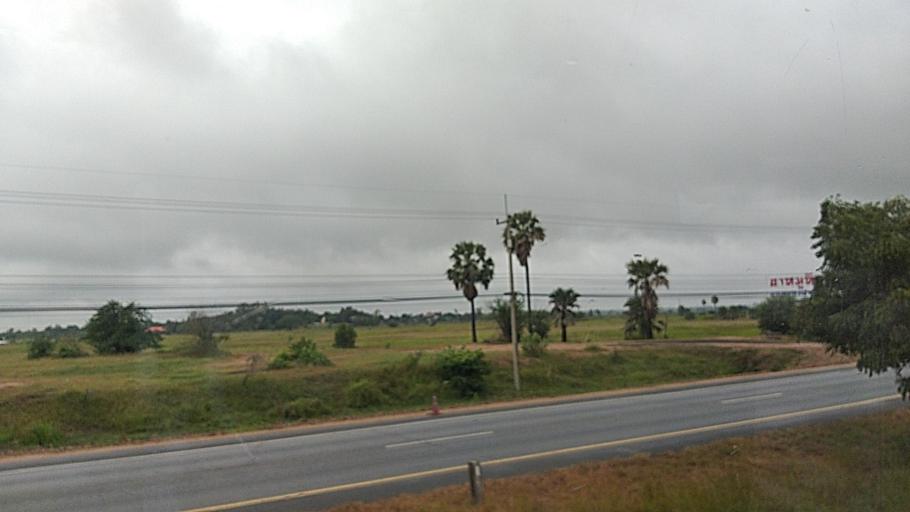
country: TH
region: Nakhon Ratchasima
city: Non Sung
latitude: 15.1200
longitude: 102.3008
